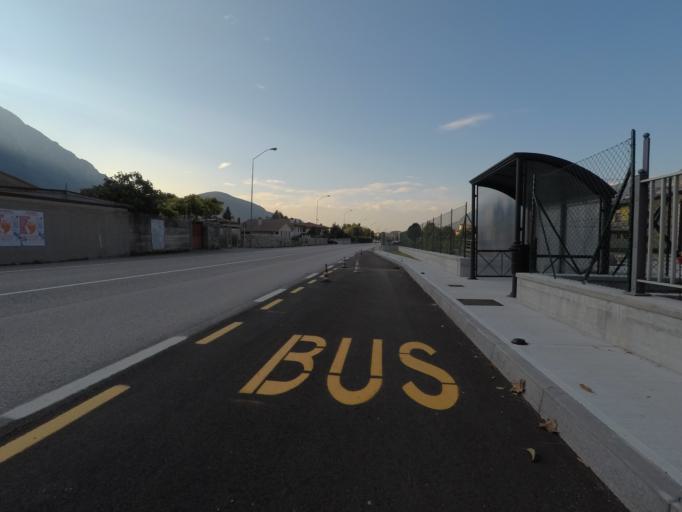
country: IT
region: Friuli Venezia Giulia
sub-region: Provincia di Udine
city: Venzone
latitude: 46.3302
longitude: 13.1368
